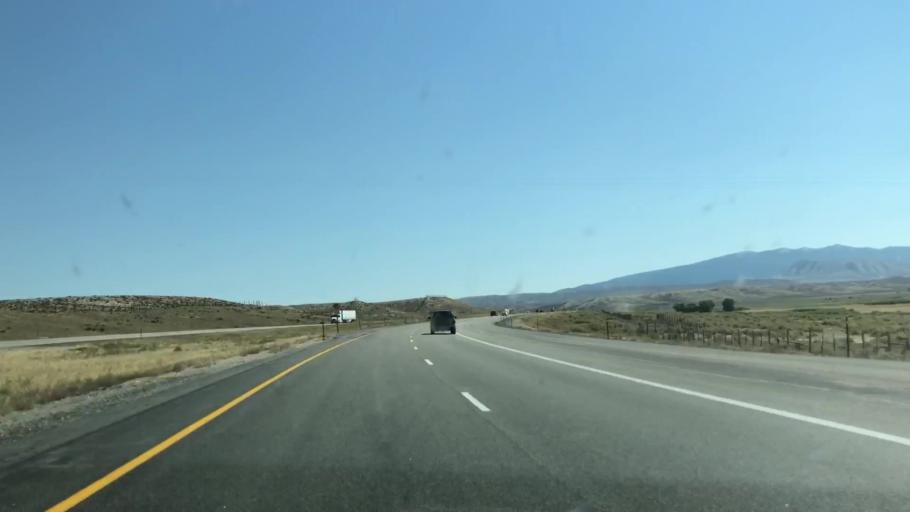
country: US
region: Wyoming
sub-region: Carbon County
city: Saratoga
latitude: 41.7419
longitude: -106.7669
